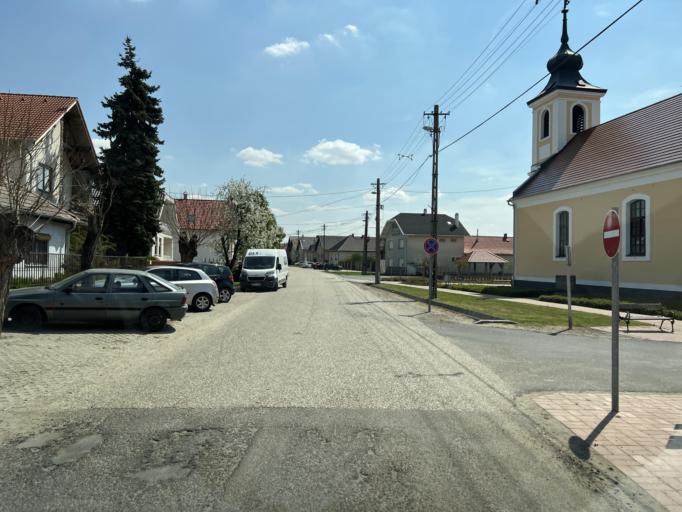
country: HU
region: Pest
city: Fot
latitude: 47.6612
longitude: 19.2280
